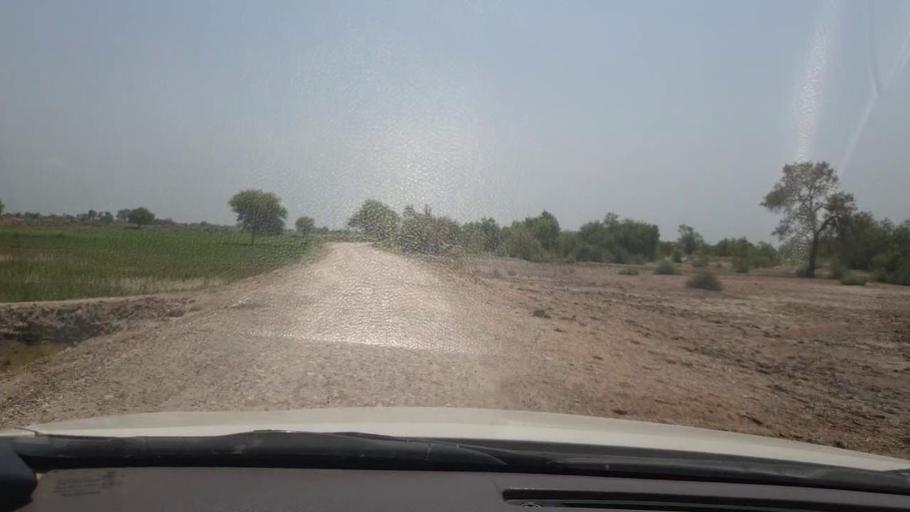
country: PK
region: Sindh
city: Garhi Yasin
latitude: 27.9202
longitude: 68.5532
